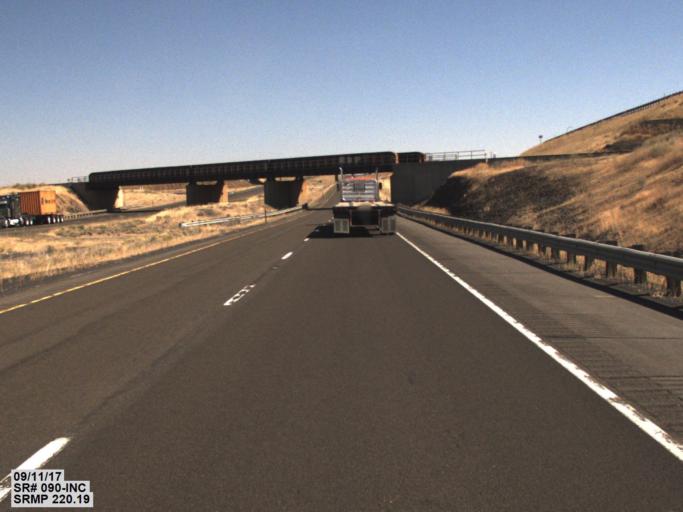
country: US
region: Washington
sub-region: Adams County
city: Ritzville
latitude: 47.1111
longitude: -118.4016
